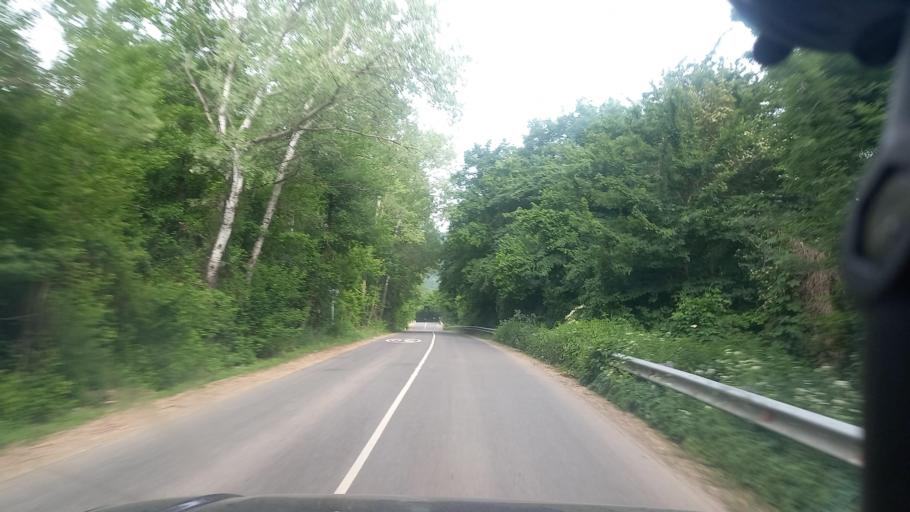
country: RU
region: Krasnodarskiy
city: Goryachiy Klyuch
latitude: 44.6028
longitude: 39.0391
